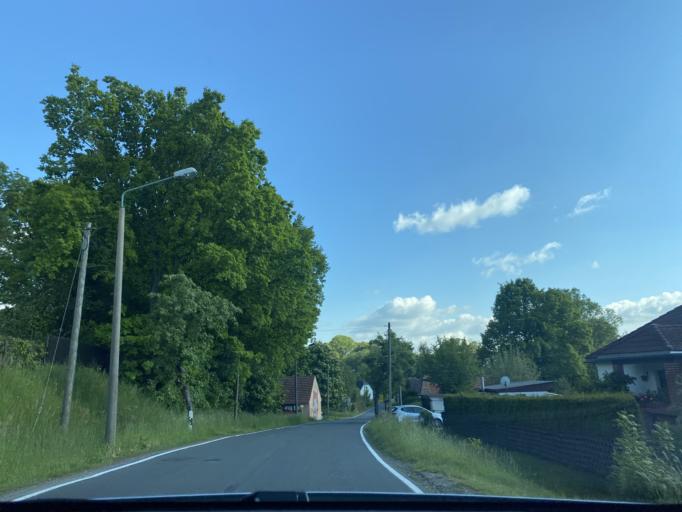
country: DE
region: Saxony
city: Markersdorf
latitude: 51.1431
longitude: 14.9242
